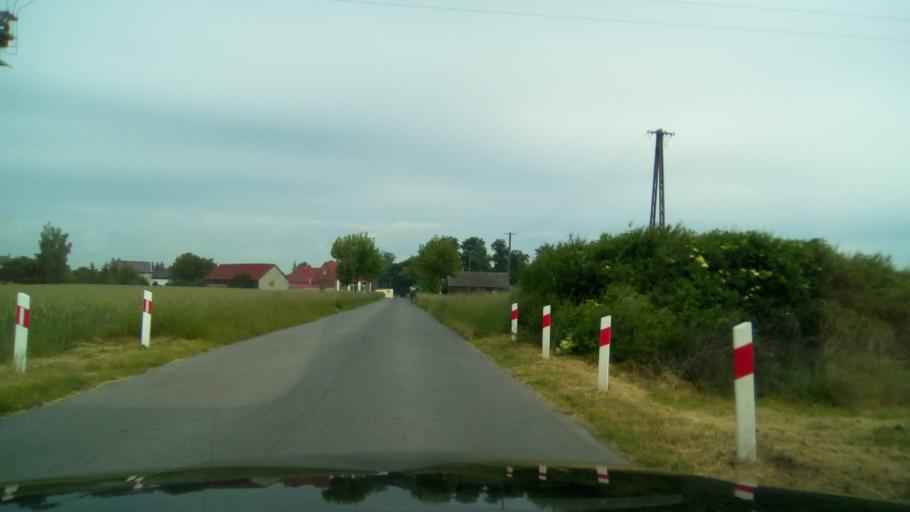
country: PL
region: Greater Poland Voivodeship
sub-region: Powiat gnieznienski
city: Mieleszyn
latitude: 52.6979
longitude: 17.4954
